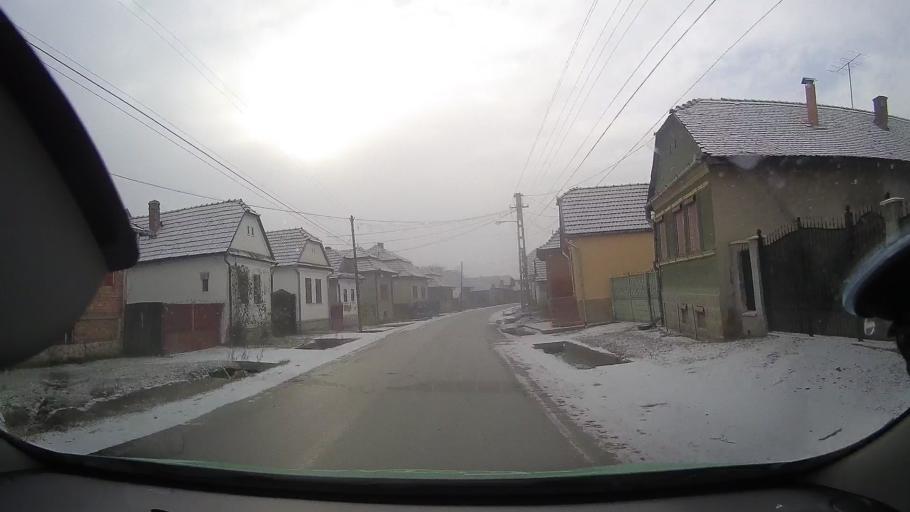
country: RO
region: Alba
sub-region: Comuna Rimetea
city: Rimetea
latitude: 46.4220
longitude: 23.5611
